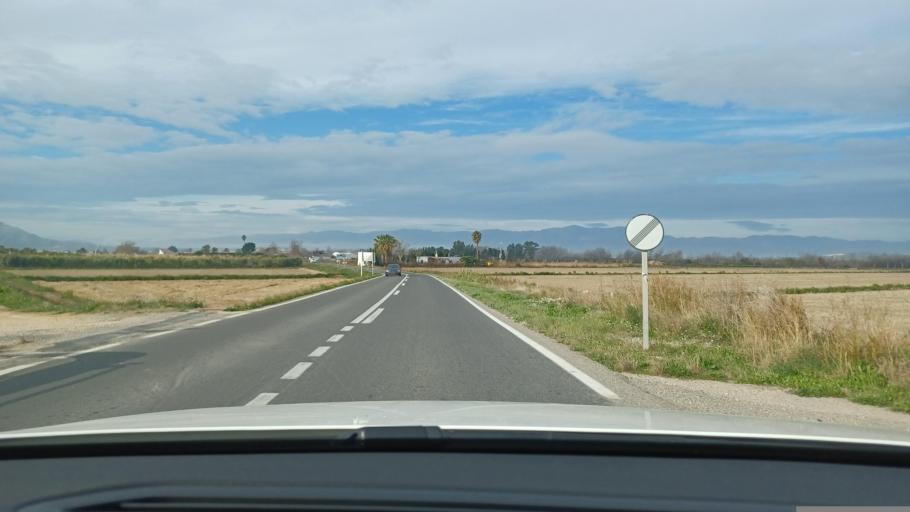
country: ES
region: Catalonia
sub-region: Provincia de Tarragona
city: Amposta
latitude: 40.7047
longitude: 0.6320
